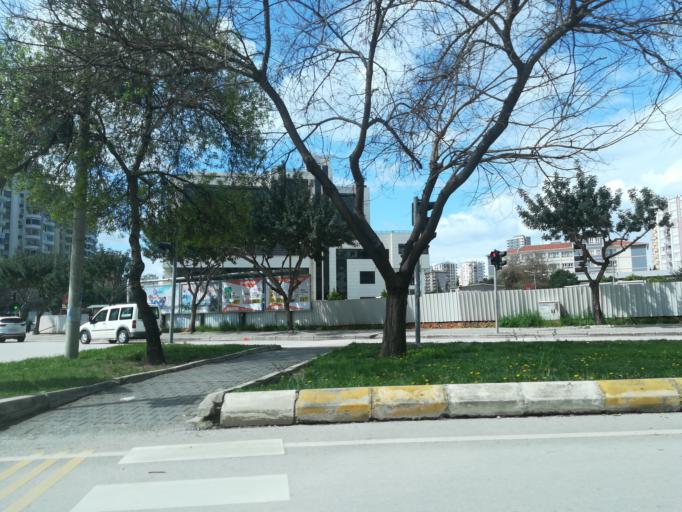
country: TR
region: Adana
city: Adana
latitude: 37.0361
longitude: 35.2984
